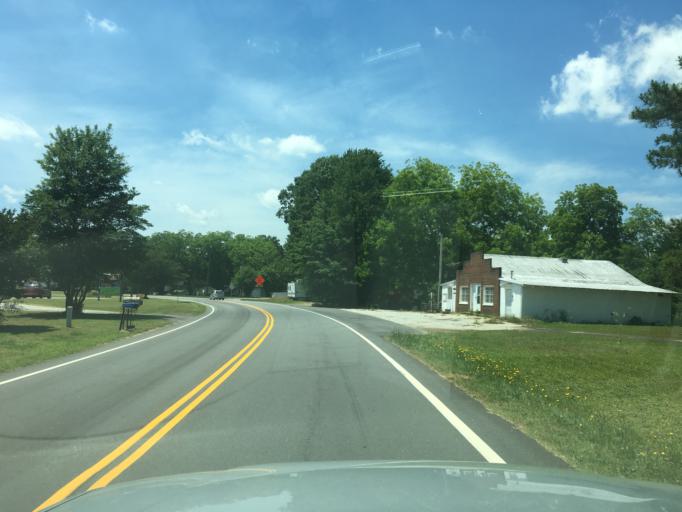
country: US
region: Georgia
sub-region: Hart County
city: Reed Creek
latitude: 34.5124
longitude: -82.9815
